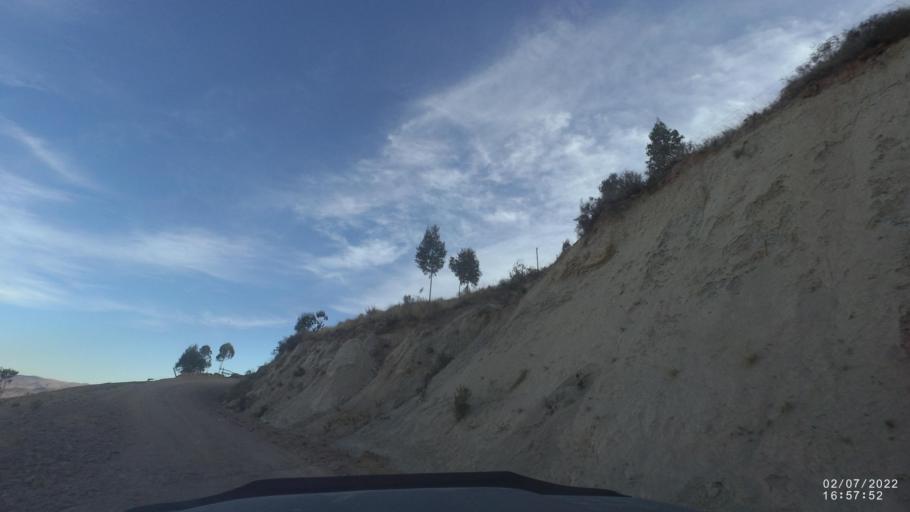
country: BO
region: Cochabamba
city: Irpa Irpa
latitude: -17.9468
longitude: -66.5464
